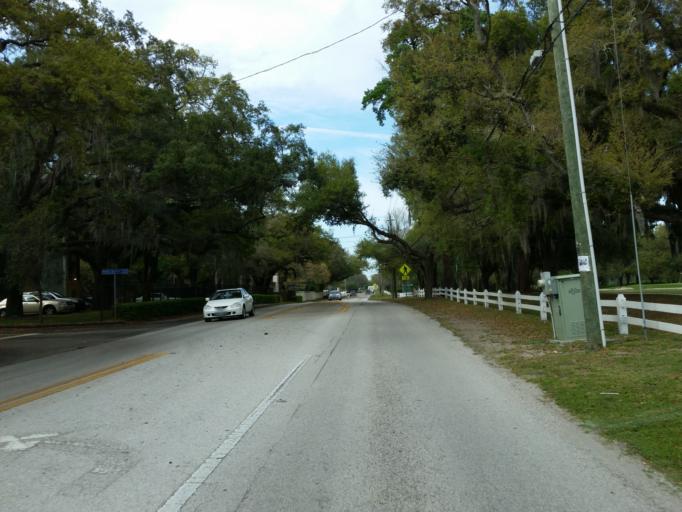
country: US
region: Florida
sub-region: Hillsborough County
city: University
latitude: 28.0709
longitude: -82.4099
